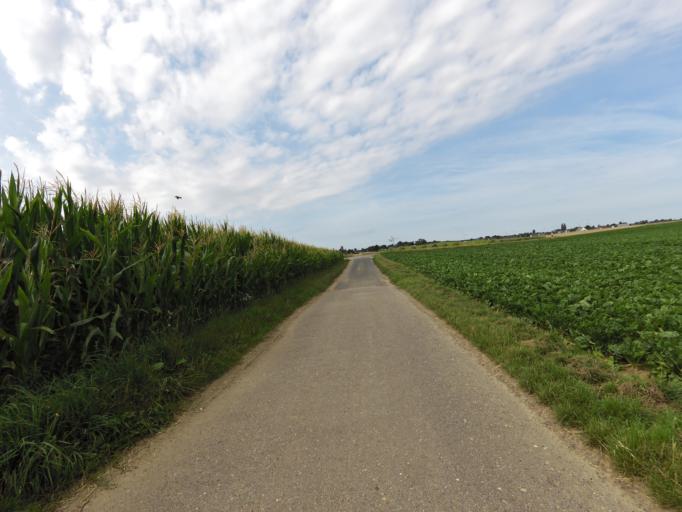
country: DE
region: North Rhine-Westphalia
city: Baesweiler
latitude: 50.9012
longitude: 6.1979
